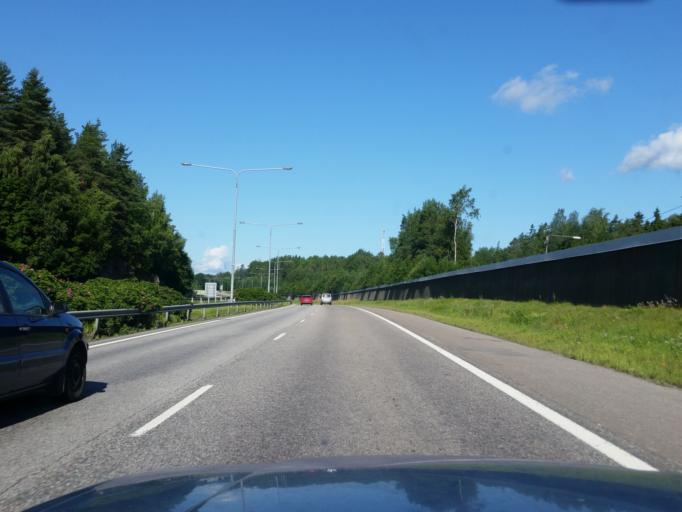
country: FI
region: Uusimaa
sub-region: Helsinki
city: Espoo
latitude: 60.2227
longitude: 24.6281
